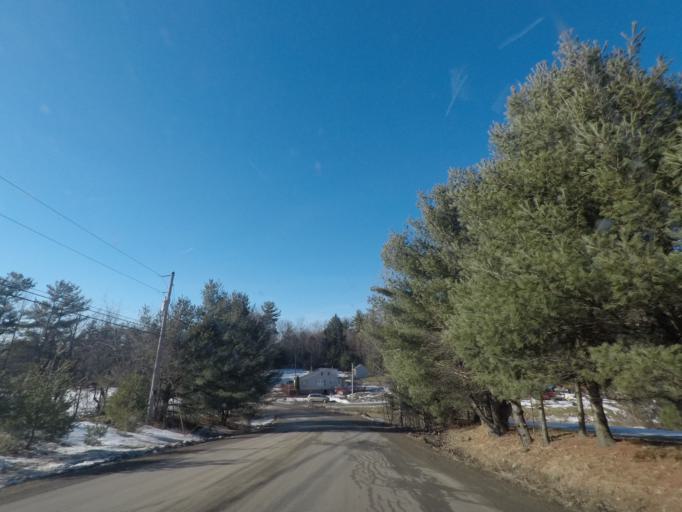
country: US
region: New York
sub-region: Rensselaer County
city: Averill Park
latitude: 42.6363
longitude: -73.5201
